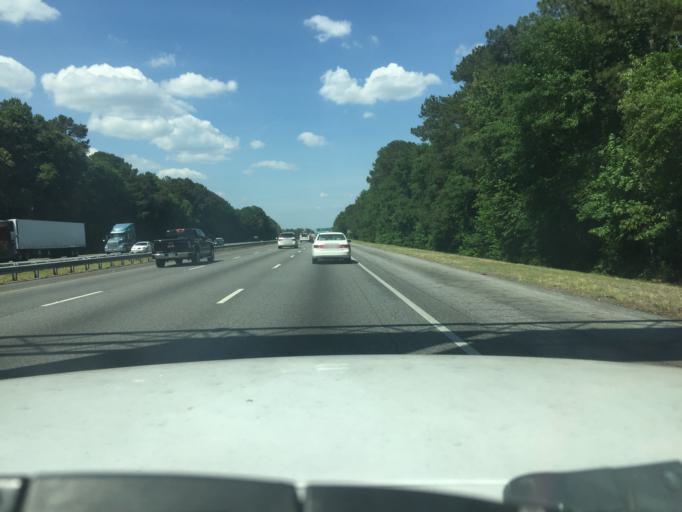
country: US
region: Georgia
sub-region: Chatham County
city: Pooler
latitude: 32.0640
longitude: -81.2510
